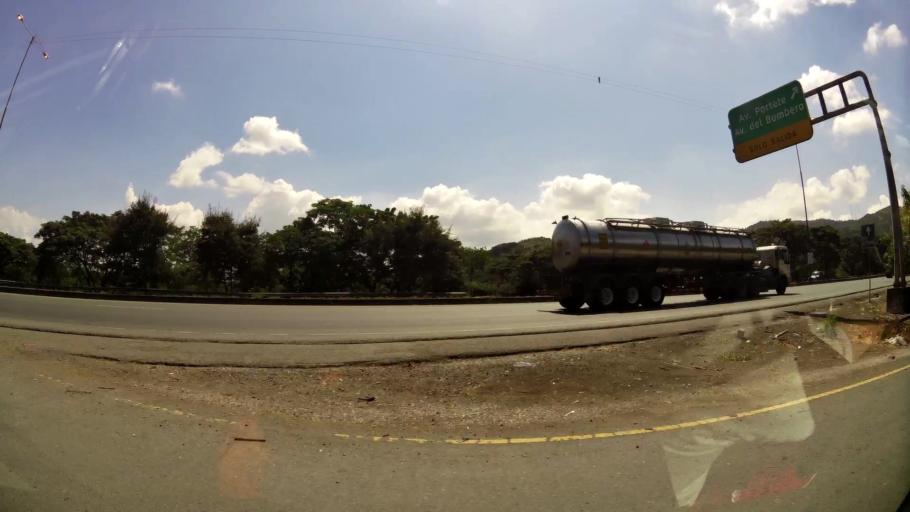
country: EC
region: Guayas
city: Santa Lucia
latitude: -2.1892
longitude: -79.9570
